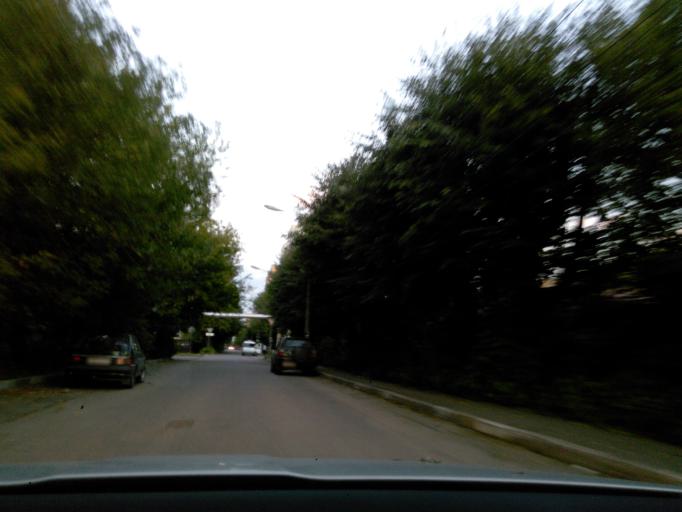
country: RU
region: Moskovskaya
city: Klin
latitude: 56.3370
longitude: 36.7228
